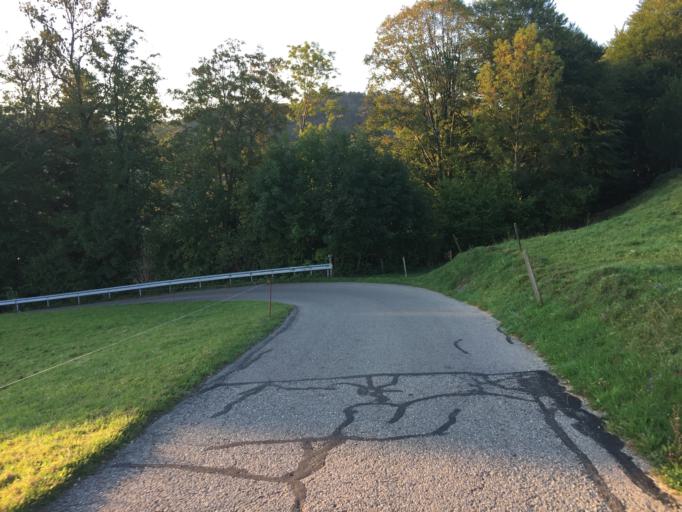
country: CH
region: Saint Gallen
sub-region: Wahlkreis Wil
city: Oberuzwil
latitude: 47.4109
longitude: 9.1385
